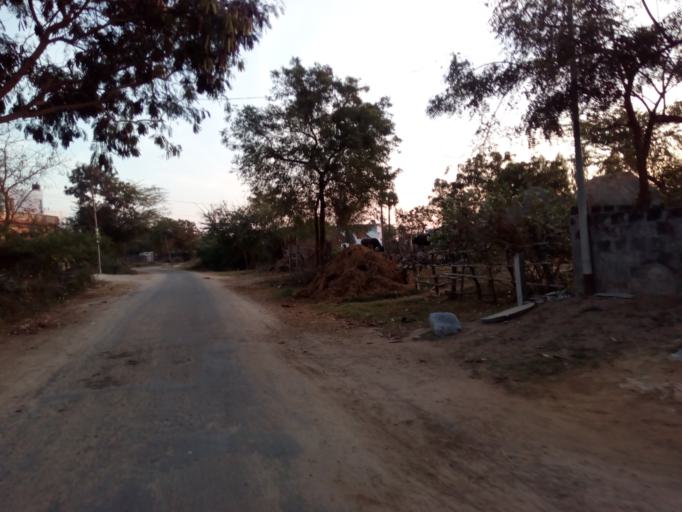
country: IN
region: Andhra Pradesh
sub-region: Prakasam
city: Vetapalem
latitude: 15.7285
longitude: 80.2504
